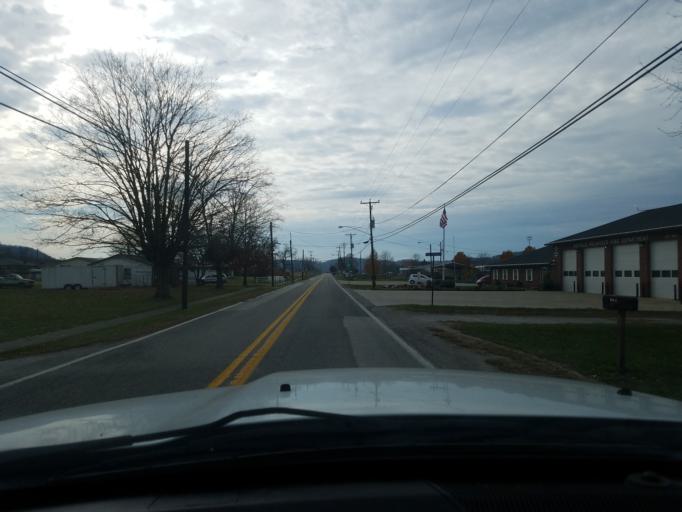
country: US
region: West Virginia
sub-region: Putnam County
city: Buffalo
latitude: 38.6088
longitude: -81.9890
